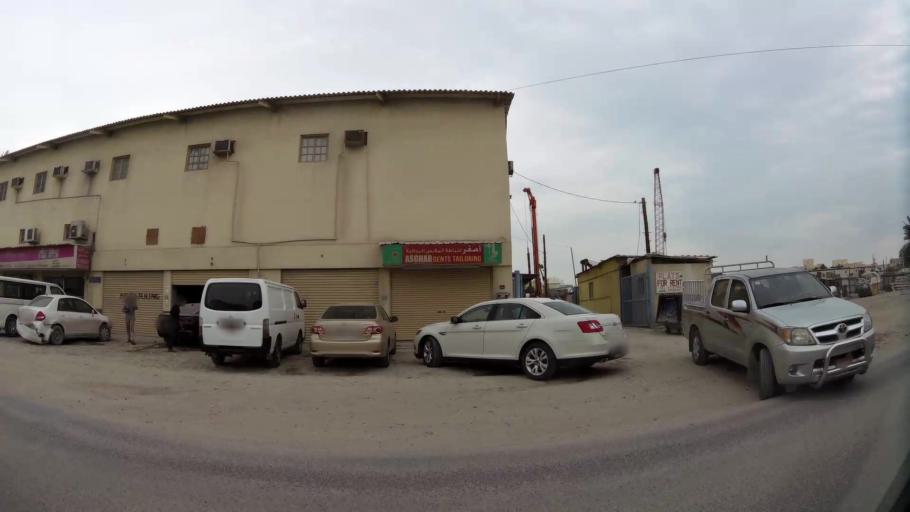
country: BH
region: Northern
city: Sitrah
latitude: 26.1403
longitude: 50.6043
